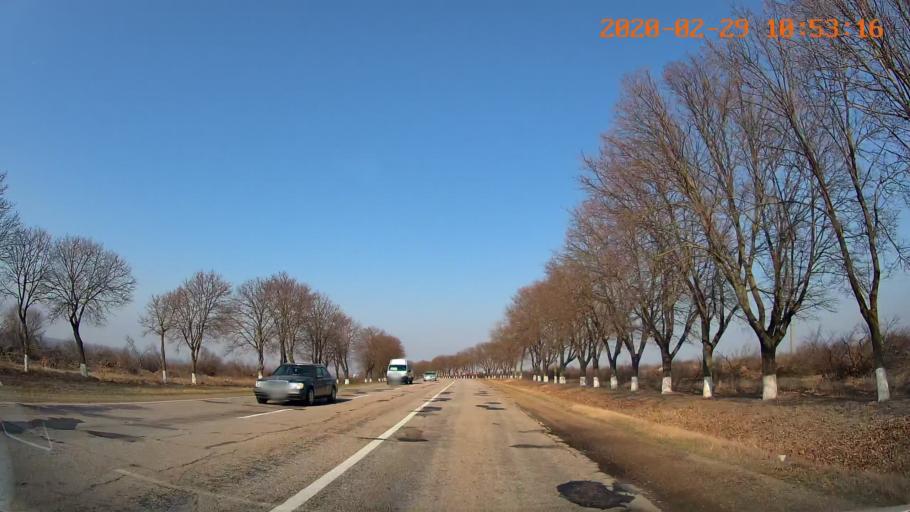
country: MD
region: Telenesti
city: Grigoriopol
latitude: 47.1140
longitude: 29.3387
